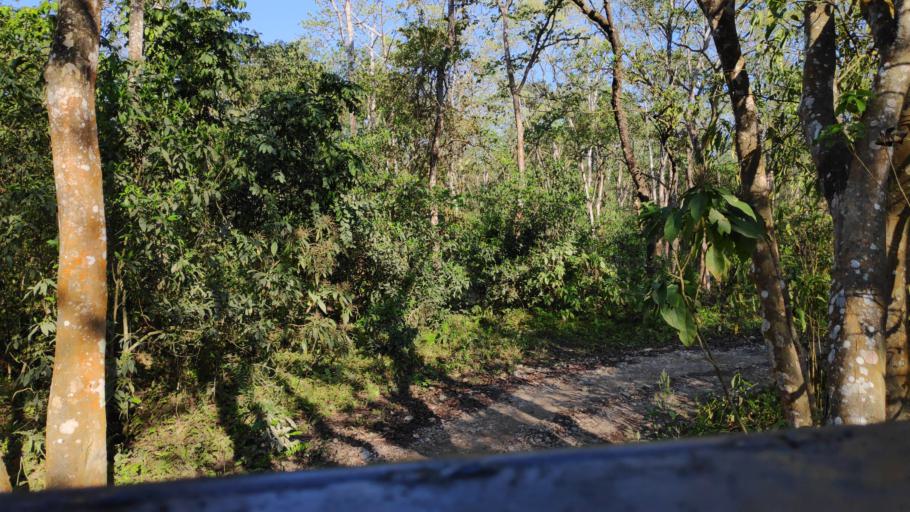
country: NP
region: Central Region
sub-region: Narayani Zone
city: Bharatpur
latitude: 27.5602
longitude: 84.5379
